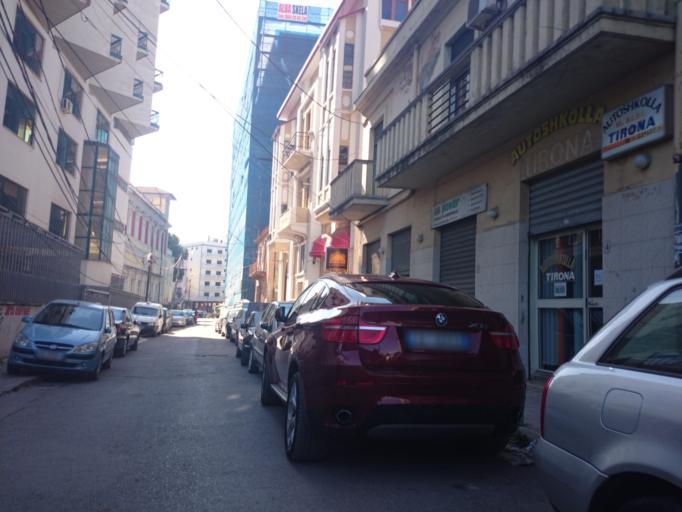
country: AL
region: Tirane
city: Tirana
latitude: 41.3286
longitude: 19.8149
